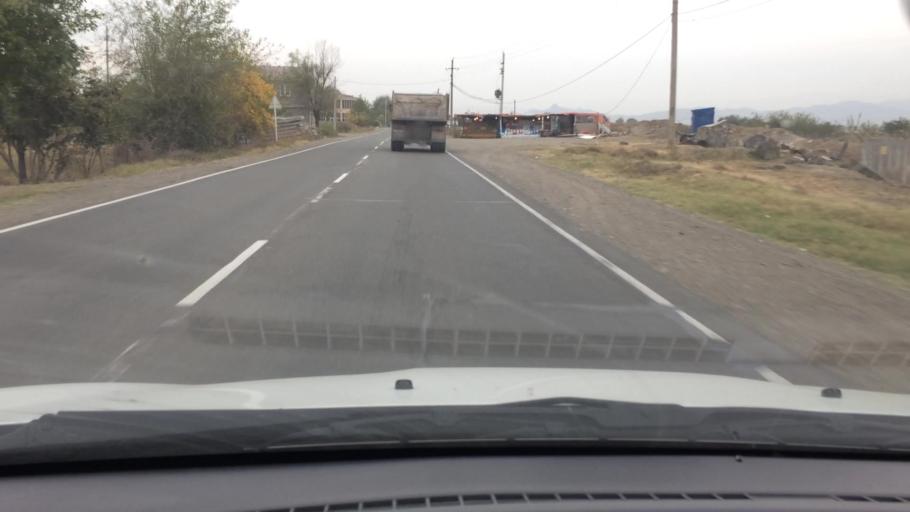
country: GE
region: Kvemo Kartli
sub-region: Marneuli
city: Marneuli
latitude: 41.4749
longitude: 44.8037
